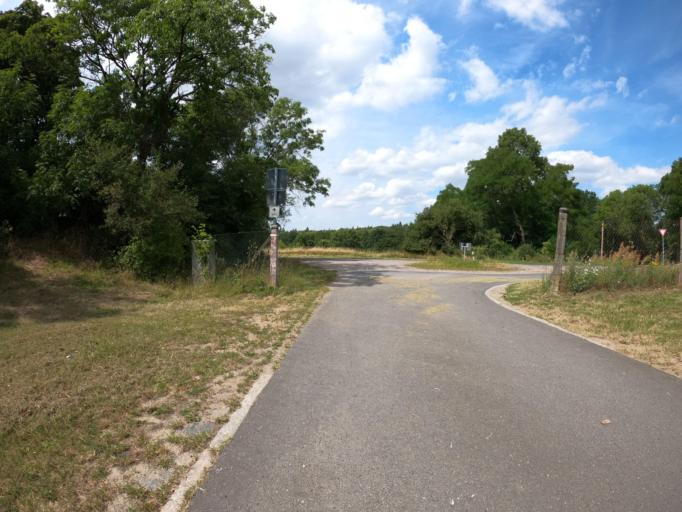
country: DE
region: Mecklenburg-Vorpommern
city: Woldegk
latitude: 53.3545
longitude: 13.5939
